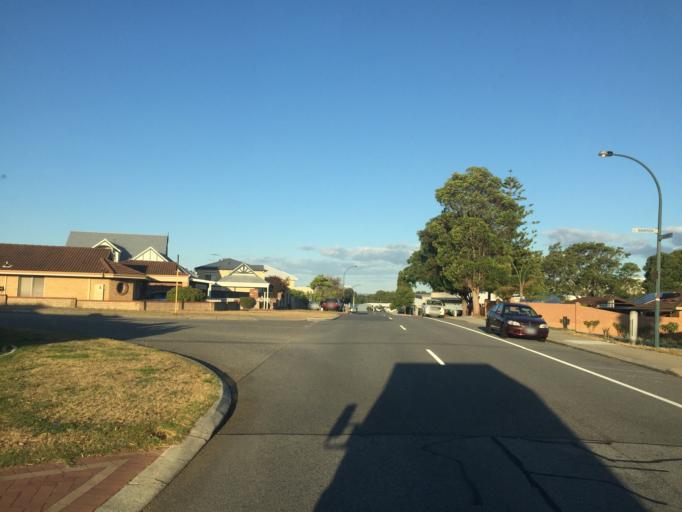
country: AU
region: Western Australia
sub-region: Belmont
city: Rivervale
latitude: -31.9549
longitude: 115.9162
